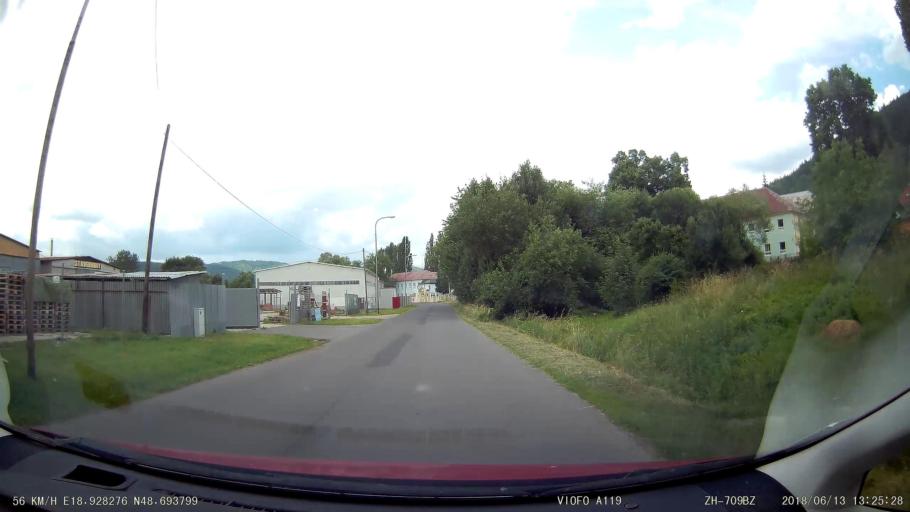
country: SK
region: Banskobystricky
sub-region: Okres Ziar nad Hronom
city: Kremnica
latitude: 48.6939
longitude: 18.9283
